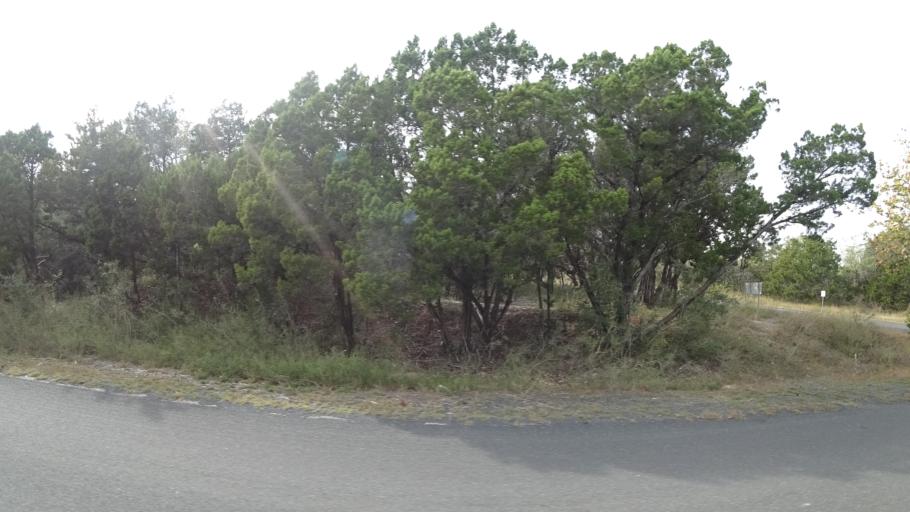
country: US
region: Texas
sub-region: Travis County
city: Hudson Bend
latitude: 30.3855
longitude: -97.9093
